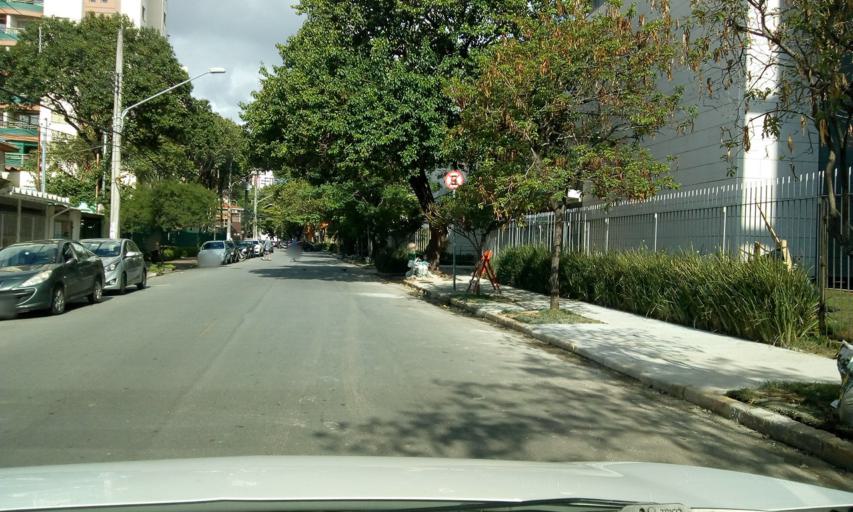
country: BR
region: Sao Paulo
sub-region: Sao Paulo
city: Sao Paulo
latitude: -23.5640
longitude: -46.6977
